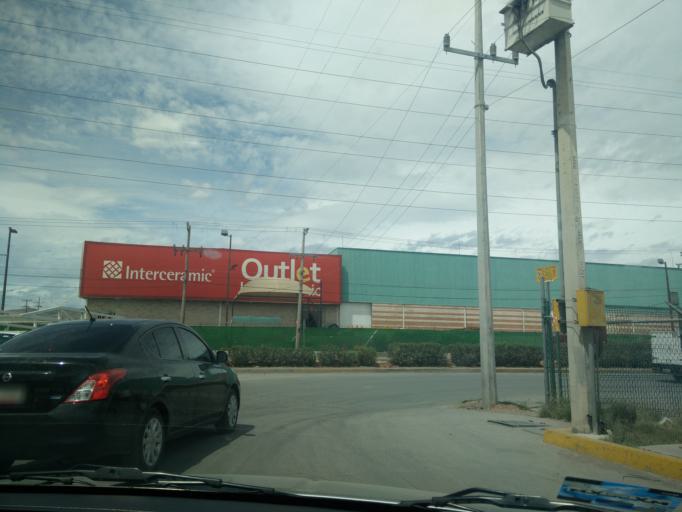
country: MX
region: Chihuahua
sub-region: Chihuahua
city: Chihuahua
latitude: 28.7130
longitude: -106.1052
